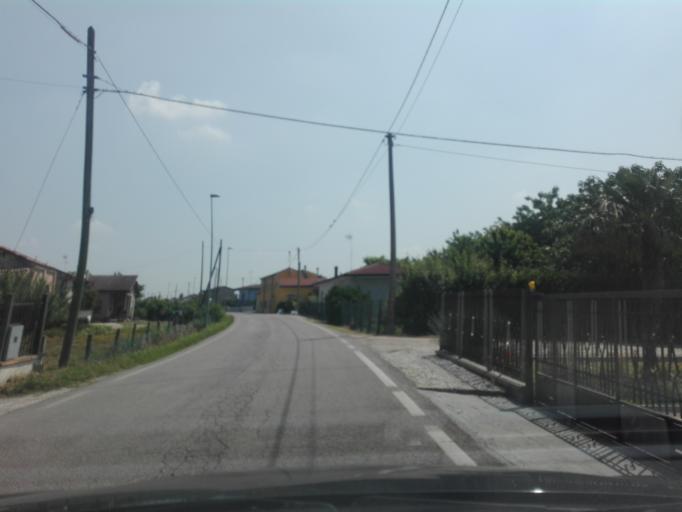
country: IT
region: Veneto
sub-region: Provincia di Rovigo
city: Lama Pezzoli
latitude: 45.0419
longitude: 11.9252
